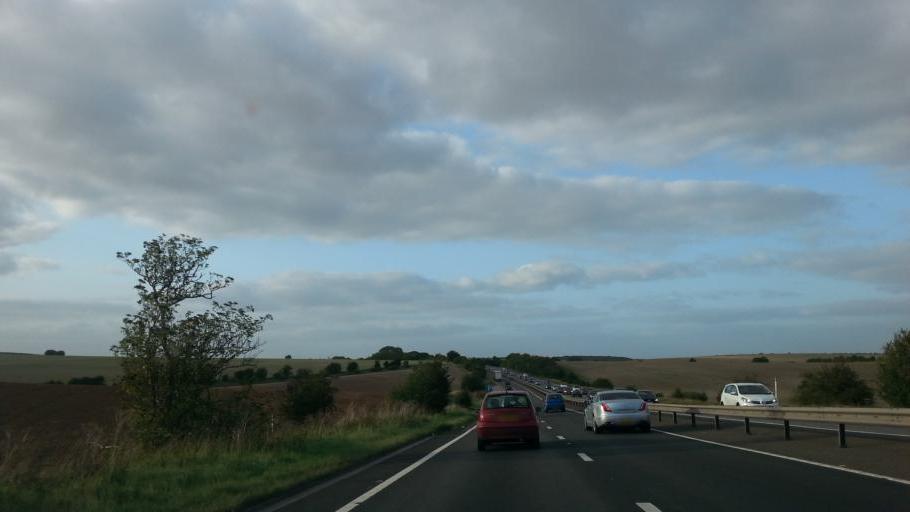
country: GB
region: England
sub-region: West Berkshire
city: Hermitage
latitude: 51.5168
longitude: -1.2909
